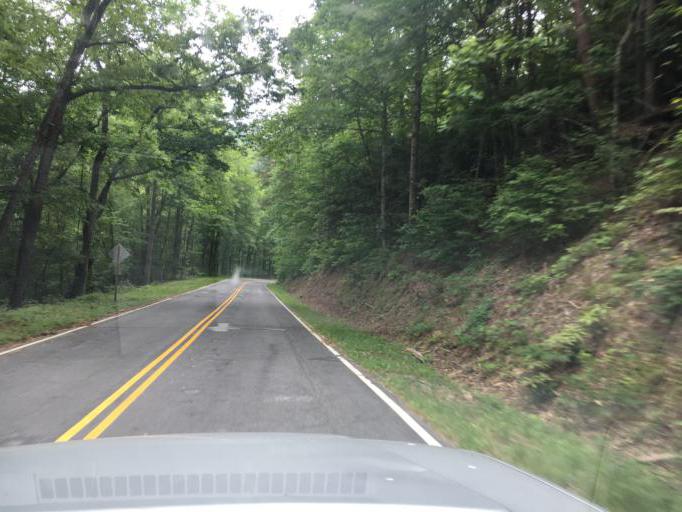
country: US
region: South Carolina
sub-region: Greenville County
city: Tigerville
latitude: 35.1640
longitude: -82.4152
